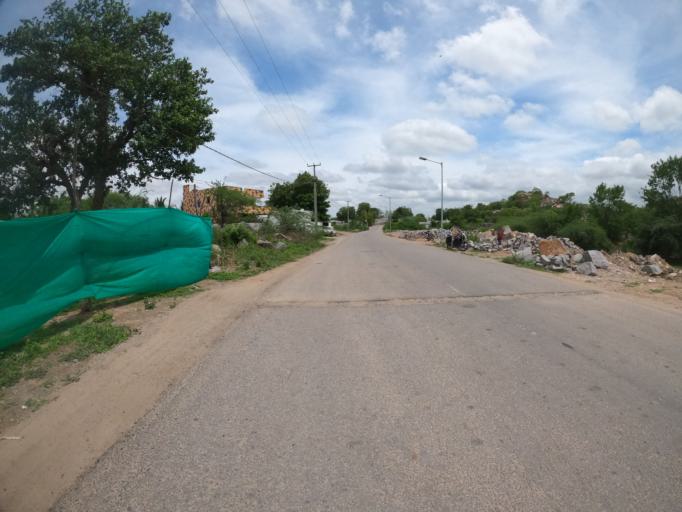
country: IN
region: Telangana
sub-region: Hyderabad
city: Hyderabad
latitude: 17.2970
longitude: 78.3792
